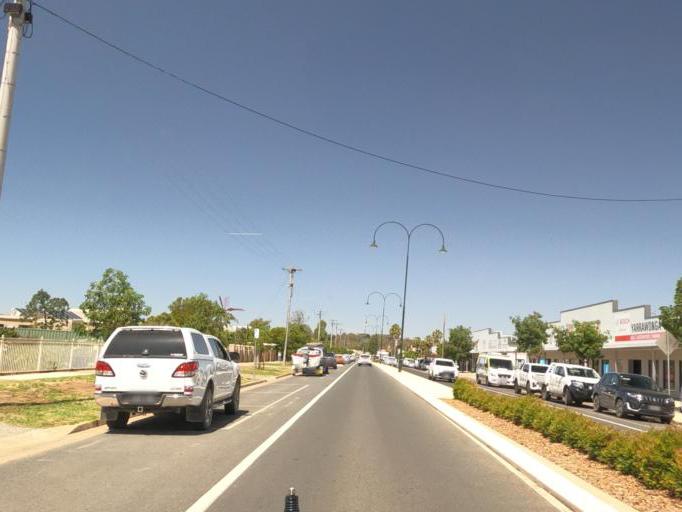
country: AU
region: New South Wales
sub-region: Corowa Shire
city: Mulwala
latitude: -35.9899
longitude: 146.0049
